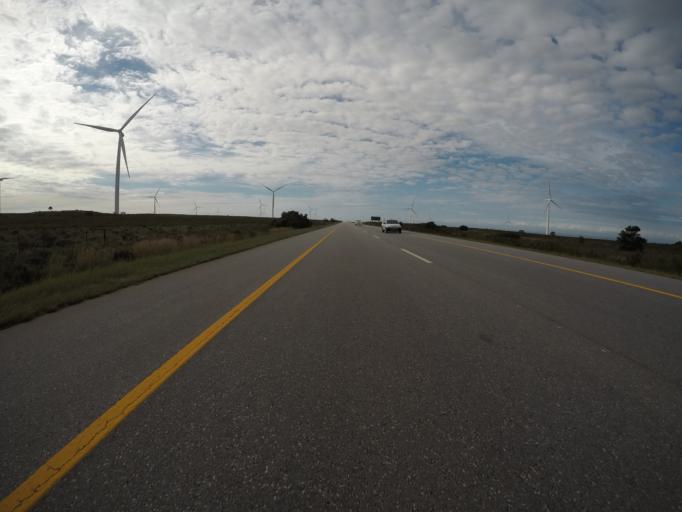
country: ZA
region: Eastern Cape
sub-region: Cacadu District Municipality
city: Kruisfontein
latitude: -34.0173
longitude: 24.8167
